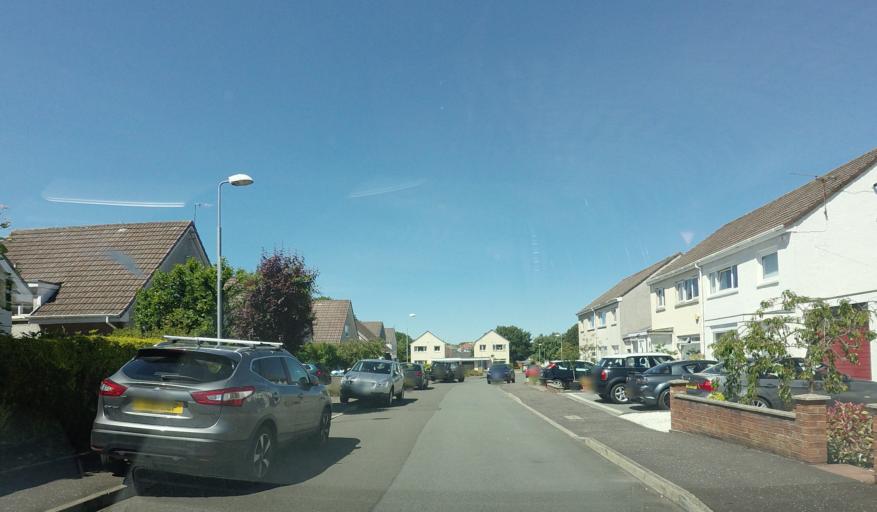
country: GB
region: Scotland
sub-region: West Lothian
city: Broxburn
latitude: 55.9311
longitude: -3.4768
